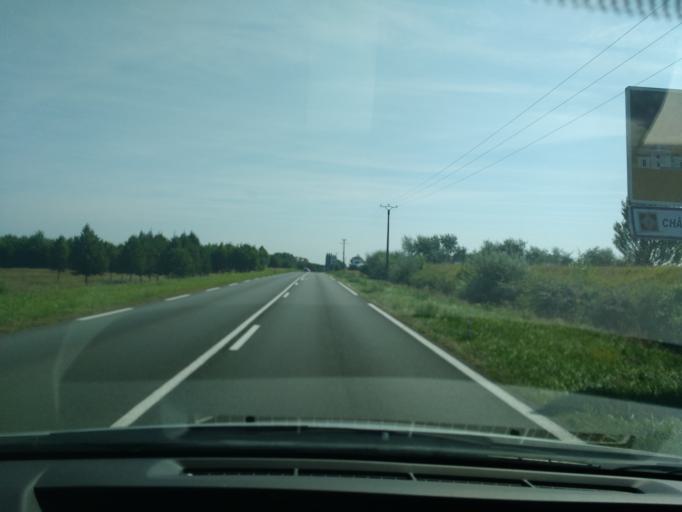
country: FR
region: Pays de la Loire
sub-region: Departement de Maine-et-Loire
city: Corne
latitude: 47.4750
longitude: -0.3461
